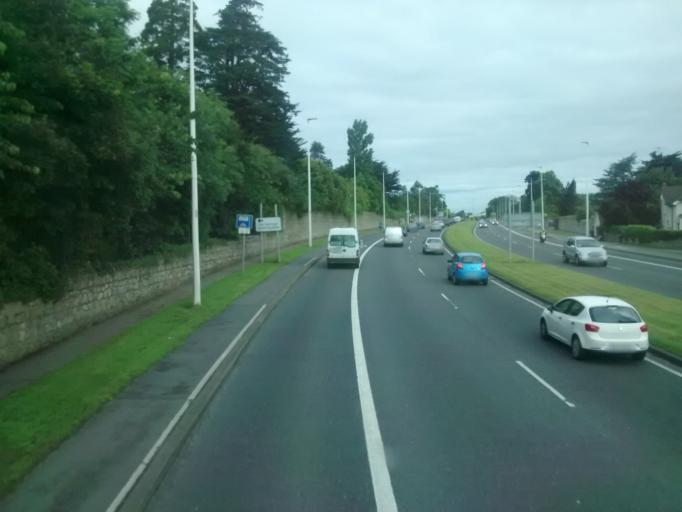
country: IE
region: Leinster
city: Foxrock
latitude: 53.2746
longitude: -6.1776
